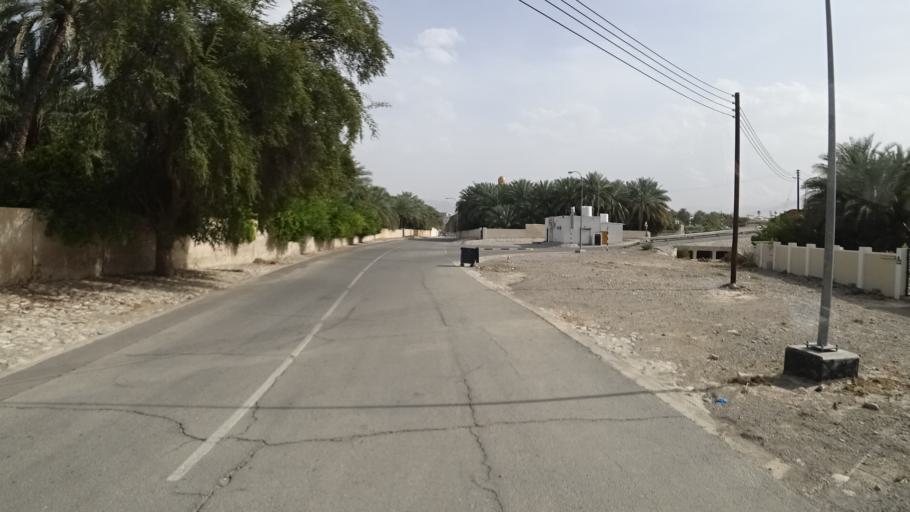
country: OM
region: Muhafazat Masqat
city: Bawshar
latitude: 23.3913
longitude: 58.5190
